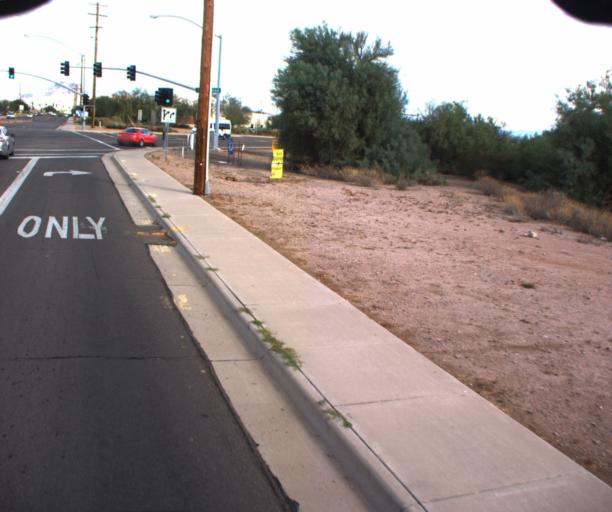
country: US
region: Arizona
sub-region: Pinal County
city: Apache Junction
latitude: 33.4186
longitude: -111.5460
